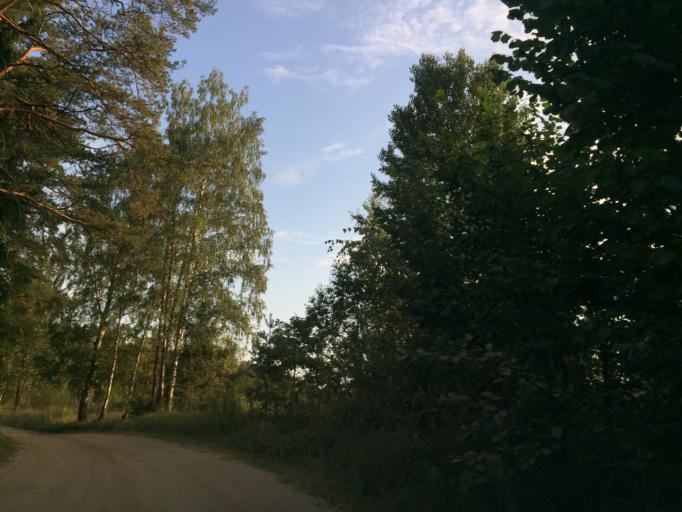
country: LV
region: Baldone
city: Baldone
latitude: 56.7626
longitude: 24.4090
